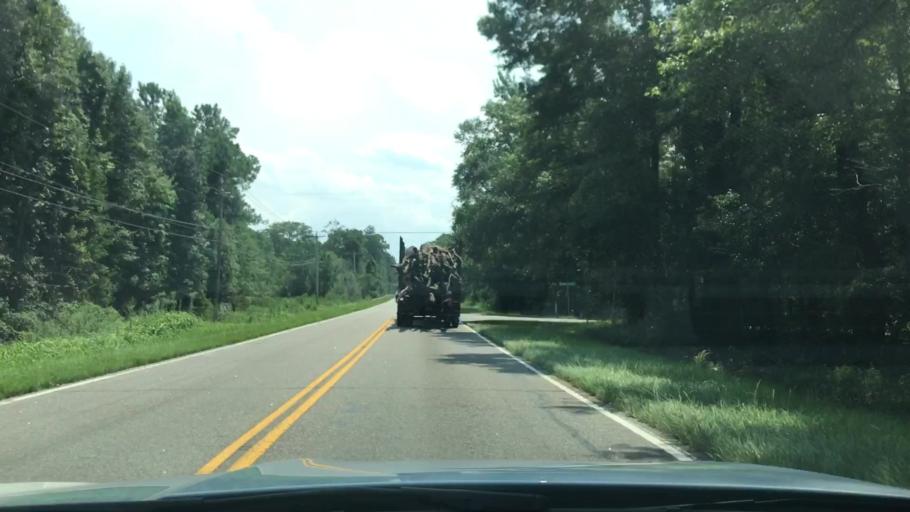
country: US
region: South Carolina
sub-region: Georgetown County
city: Georgetown
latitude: 33.4710
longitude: -79.2794
